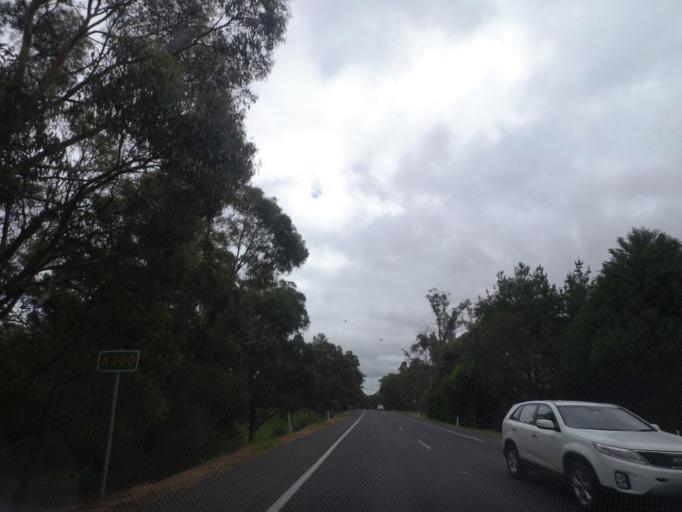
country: AU
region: Victoria
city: Brown Hill
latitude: -37.4364
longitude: 143.8920
